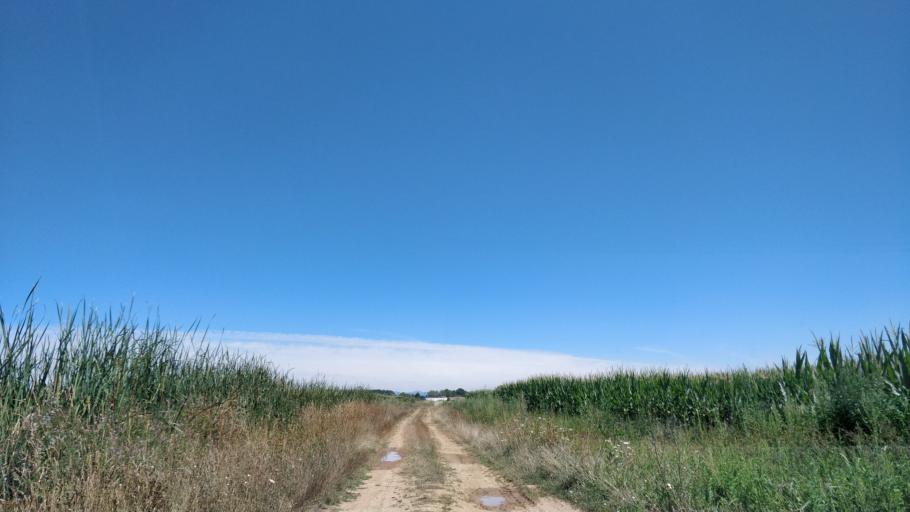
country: ES
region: Castille and Leon
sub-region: Provincia de Leon
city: Bustillo del Paramo
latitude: 42.4686
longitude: -5.8138
